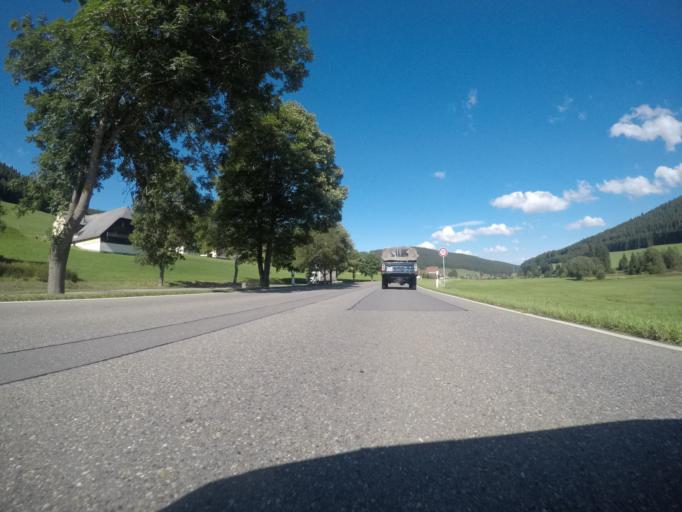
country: DE
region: Baden-Wuerttemberg
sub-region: Freiburg Region
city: Furtwangen im Schwarzwald
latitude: 48.0467
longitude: 8.2367
